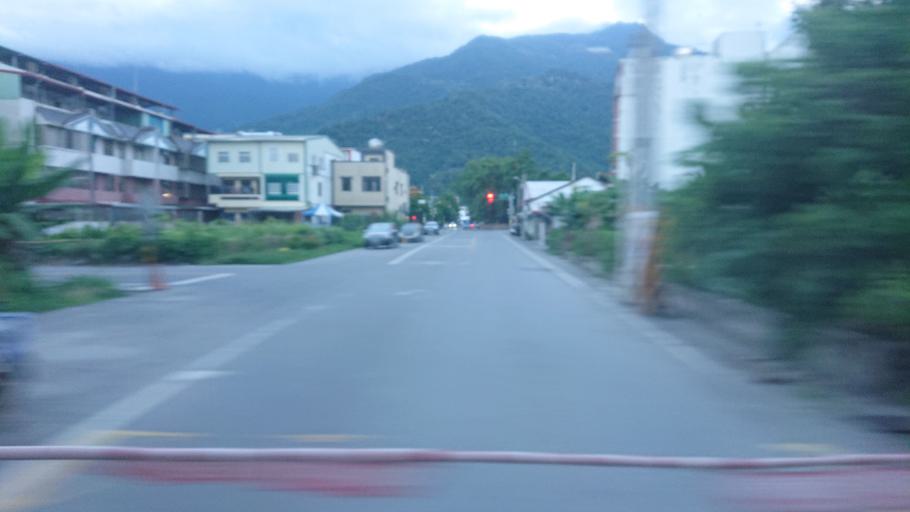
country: TW
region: Taiwan
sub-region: Taitung
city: Taitung
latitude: 23.0492
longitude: 121.1656
